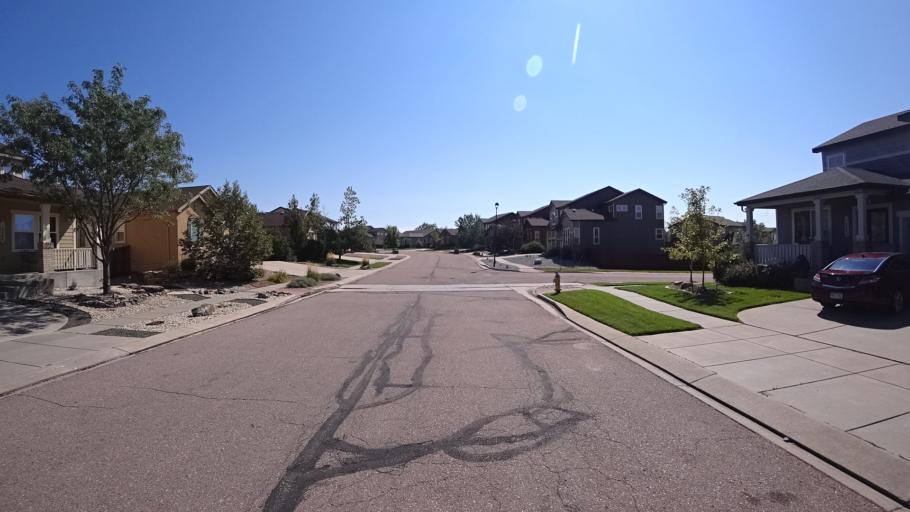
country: US
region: Colorado
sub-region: El Paso County
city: Cimarron Hills
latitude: 38.9186
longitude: -104.6994
